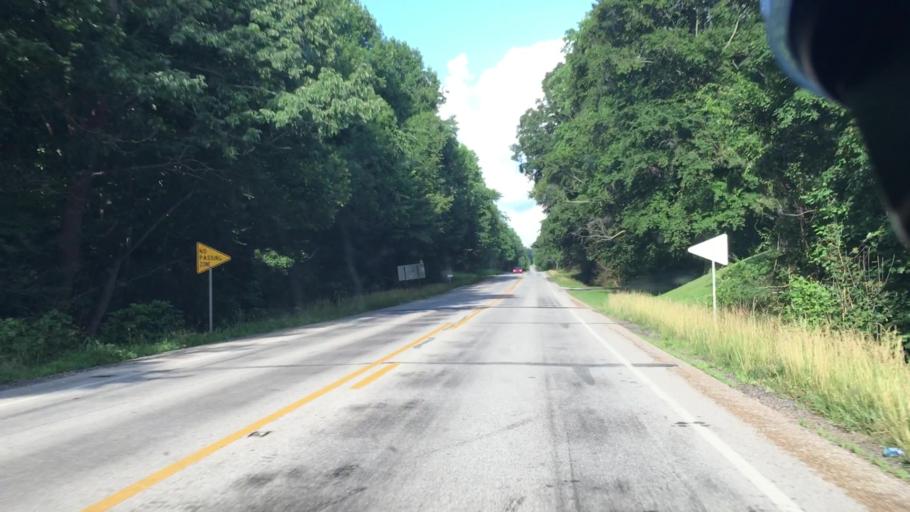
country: US
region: Kentucky
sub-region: Hancock County
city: Lewisport
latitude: 38.0013
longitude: -86.8479
